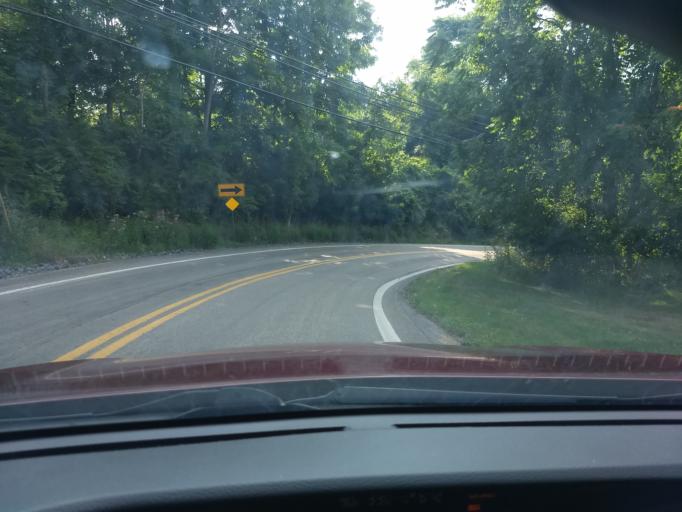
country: US
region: Pennsylvania
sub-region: Westmoreland County
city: Lower Burrell
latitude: 40.5375
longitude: -79.7607
